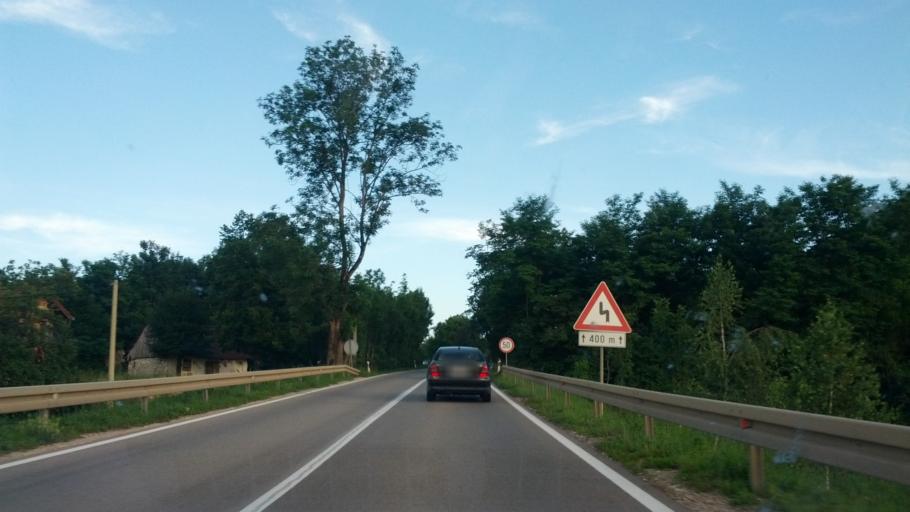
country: BA
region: Federation of Bosnia and Herzegovina
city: Izacic
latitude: 44.8901
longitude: 15.7246
